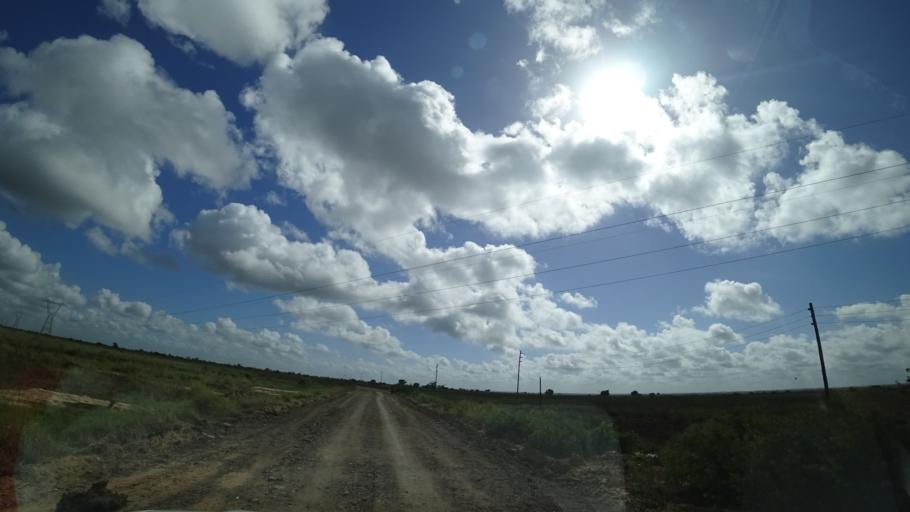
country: MZ
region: Sofala
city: Dondo
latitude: -19.4599
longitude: 34.5631
